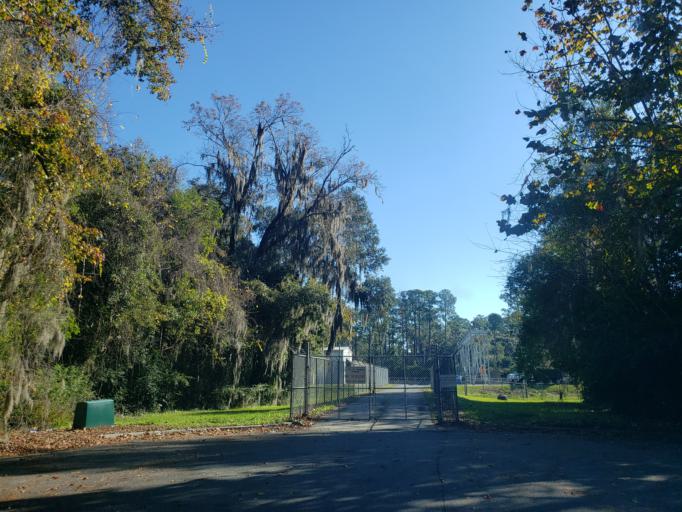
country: US
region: Georgia
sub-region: Chatham County
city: Isle of Hope
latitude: 31.9955
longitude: -81.1020
